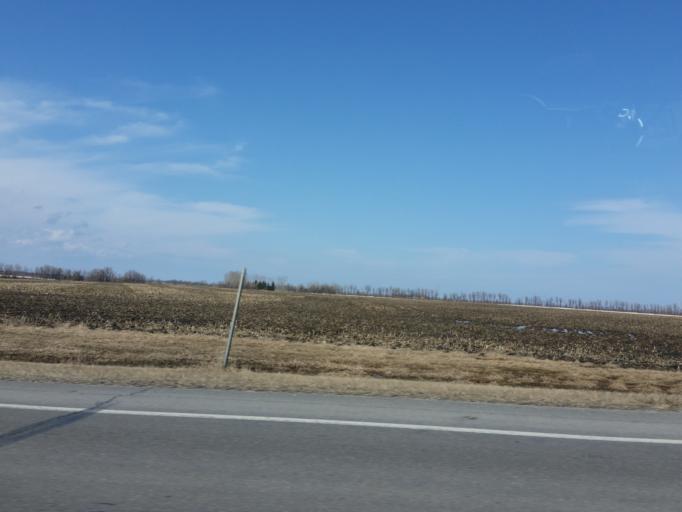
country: US
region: North Dakota
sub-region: Walsh County
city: Grafton
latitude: 48.2101
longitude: -97.3461
